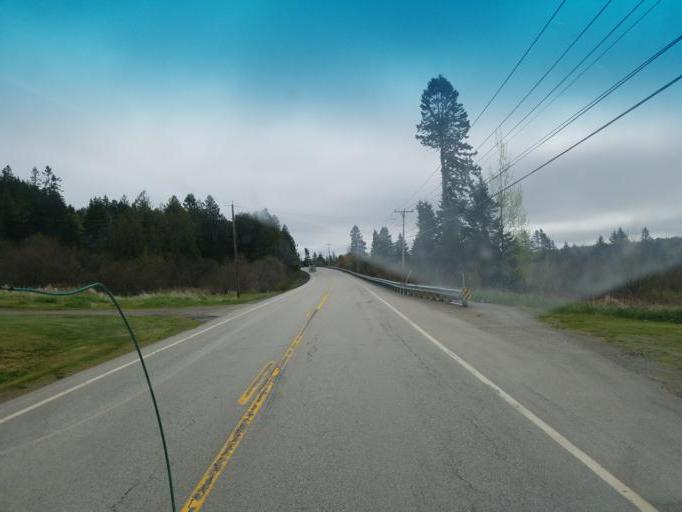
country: US
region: Maine
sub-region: Washington County
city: Eastport
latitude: 44.8090
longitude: -67.0881
